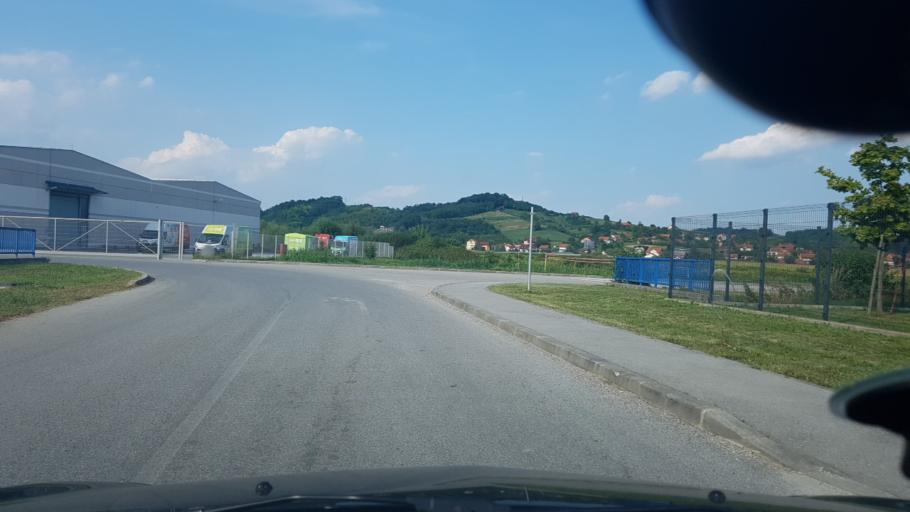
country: HR
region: Krapinsko-Zagorska
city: Zabok
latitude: 46.0731
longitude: 15.9107
